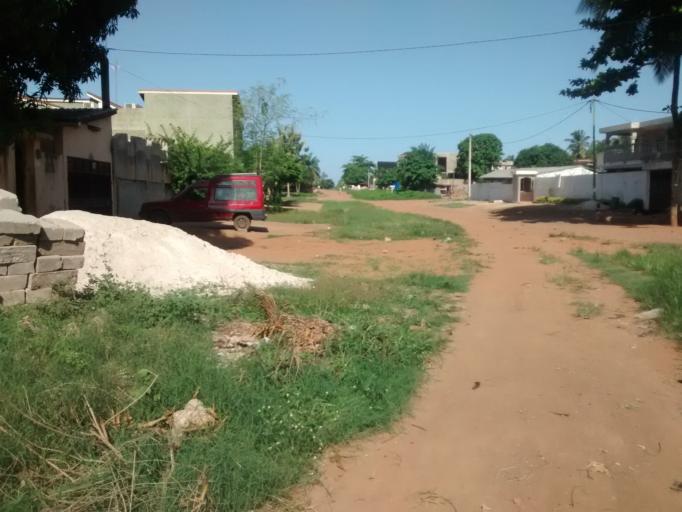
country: TG
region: Maritime
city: Lome
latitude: 6.1757
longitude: 1.1857
